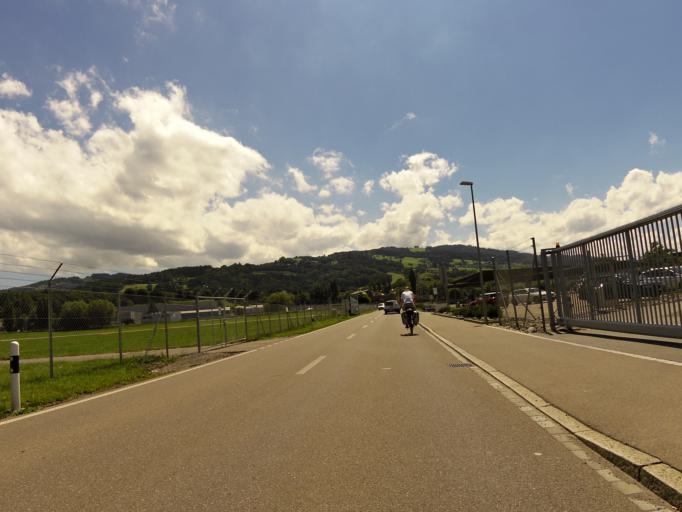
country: CH
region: Saint Gallen
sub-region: Wahlkreis Rheintal
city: Rheineck
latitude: 47.4876
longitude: 9.5504
